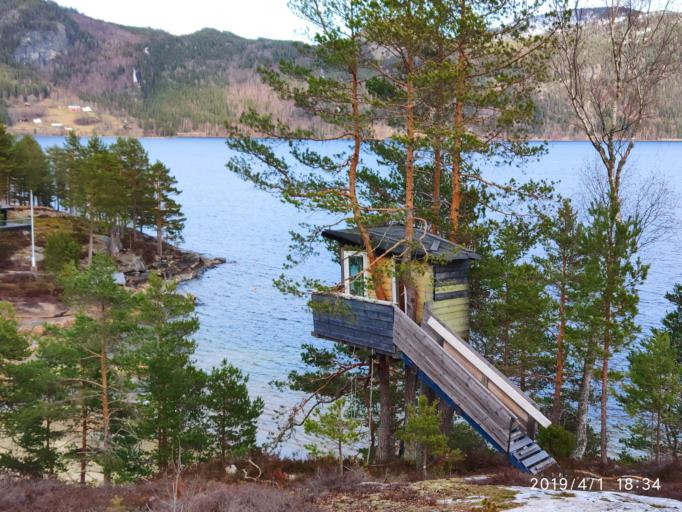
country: NO
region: Telemark
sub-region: Nissedal
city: Treungen
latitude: 59.1180
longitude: 8.4778
